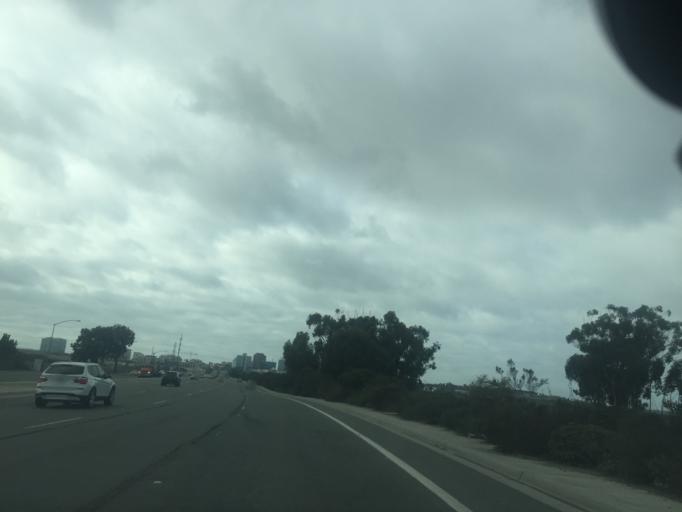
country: US
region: California
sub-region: San Diego County
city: La Jolla
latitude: 32.8770
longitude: -117.1878
